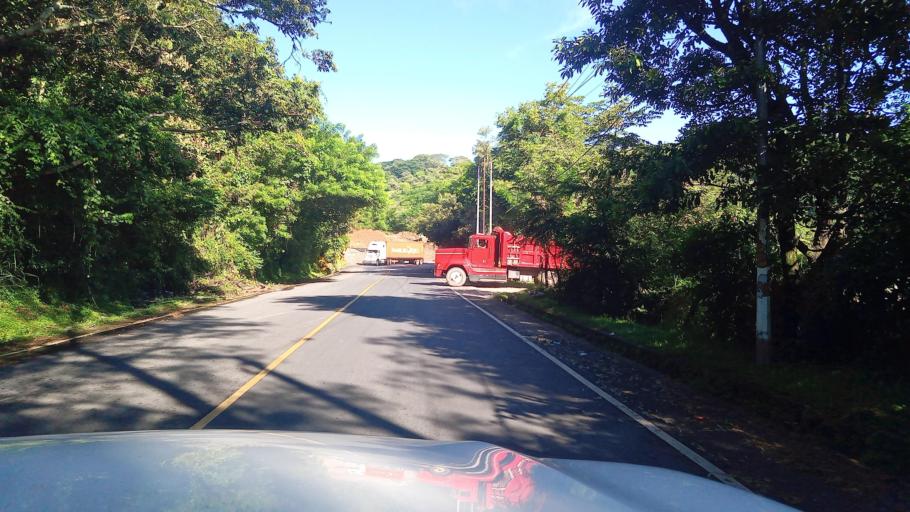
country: HN
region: Ocotepeque
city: Antigua Ocotepeque
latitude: 14.3217
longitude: -89.1769
